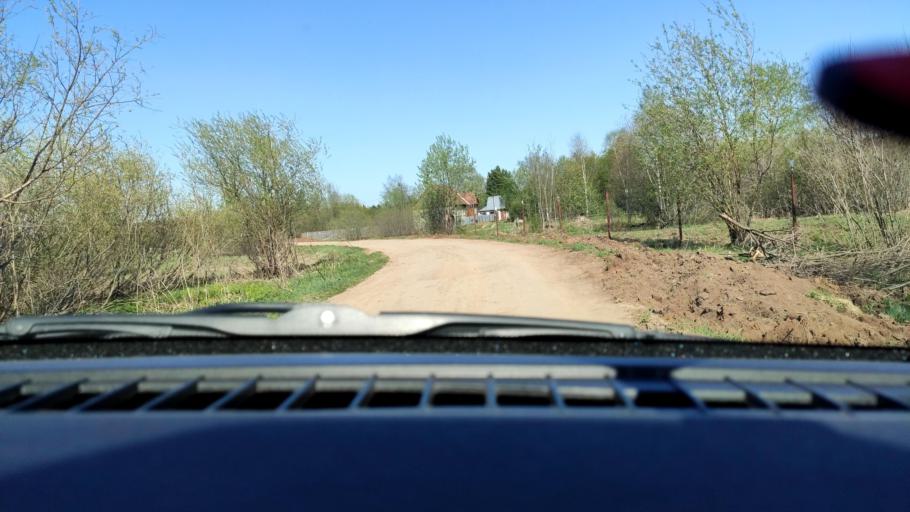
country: RU
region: Perm
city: Overyata
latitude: 58.0800
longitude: 55.9776
